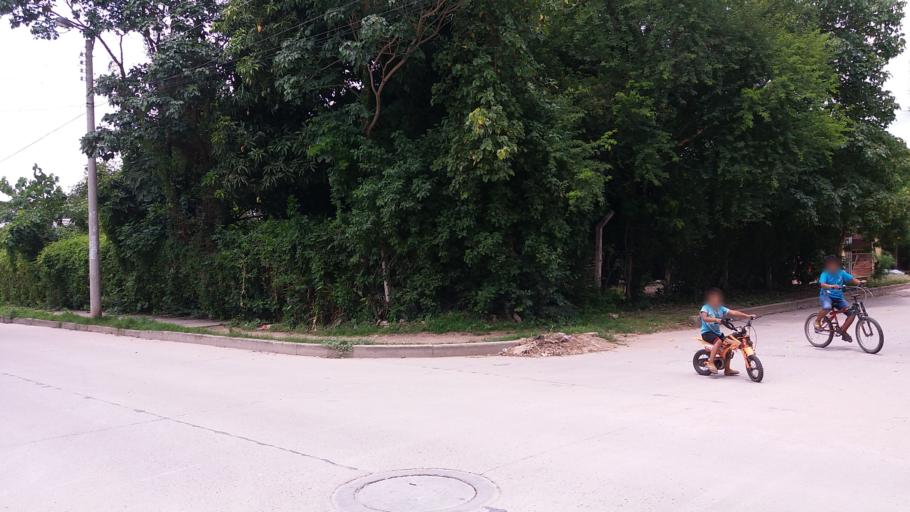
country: BO
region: Tarija
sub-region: Provincia Gran Chaco
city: Yacuiba
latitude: -22.0194
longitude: -63.6731
